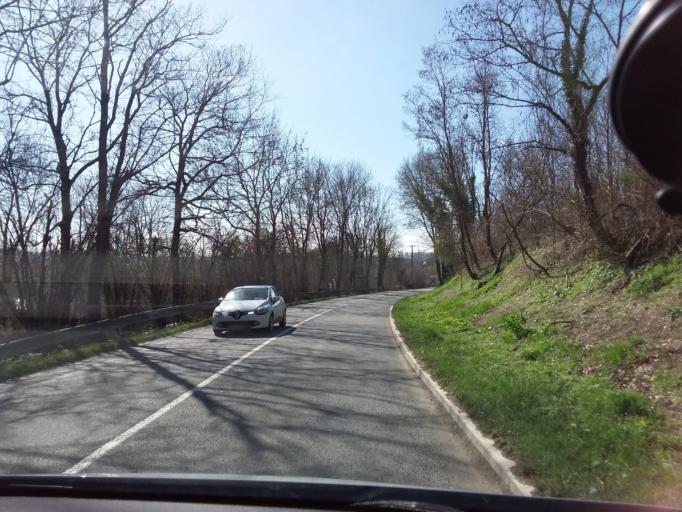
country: FR
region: Picardie
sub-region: Departement de l'Aisne
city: Guignicourt
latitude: 49.4353
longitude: 4.0325
